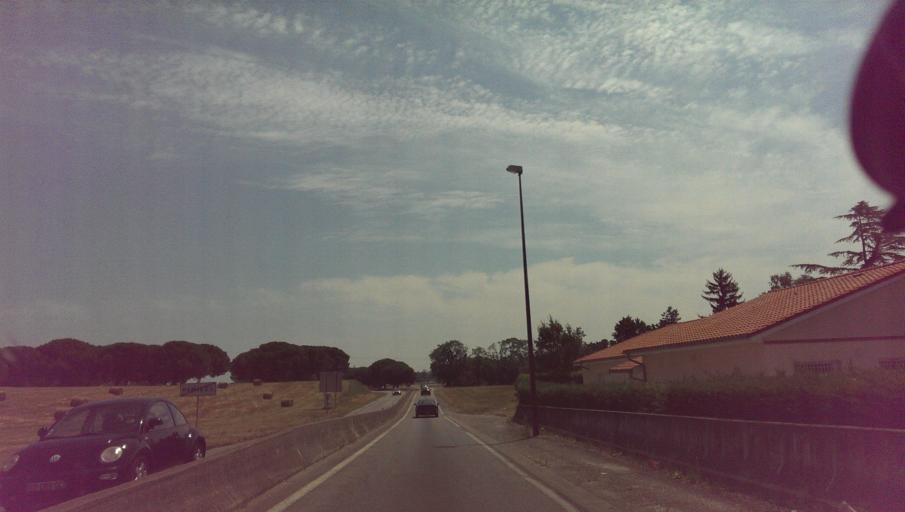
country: FR
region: Midi-Pyrenees
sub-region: Departement de l'Ariege
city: Saint-Jean-du-Falga
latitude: 43.1026
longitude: 1.6296
